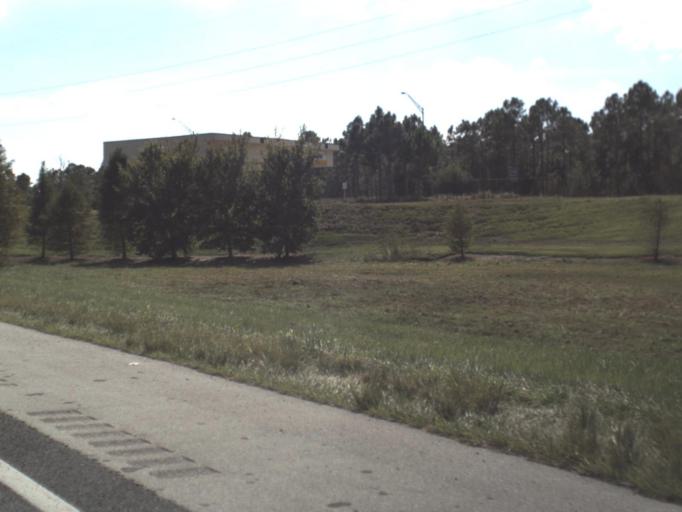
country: US
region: Florida
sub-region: Polk County
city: Citrus Ridge
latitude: 28.2948
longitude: -81.6025
